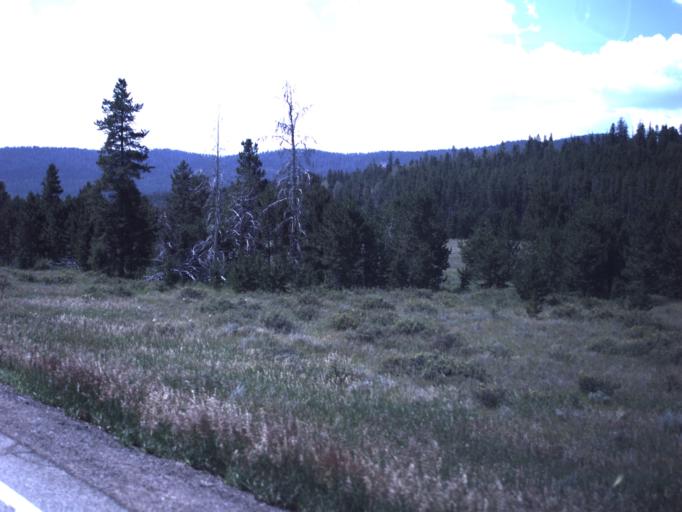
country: US
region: Utah
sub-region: Uintah County
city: Maeser
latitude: 40.7731
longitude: -109.4713
